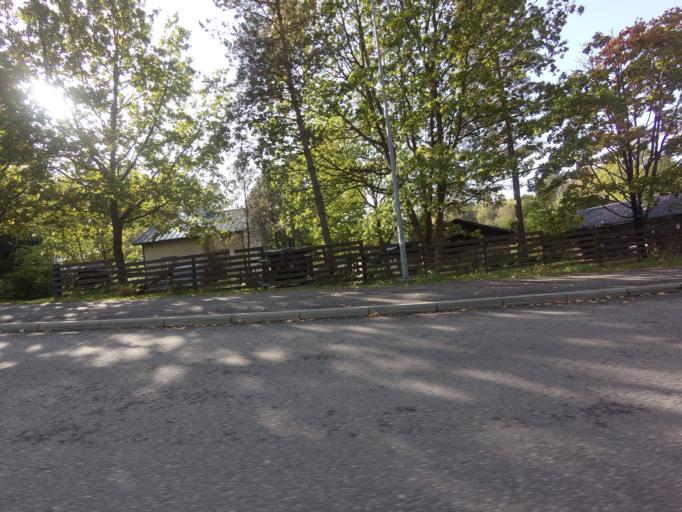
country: FI
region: Uusimaa
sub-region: Helsinki
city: Espoo
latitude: 60.1786
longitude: 24.6489
